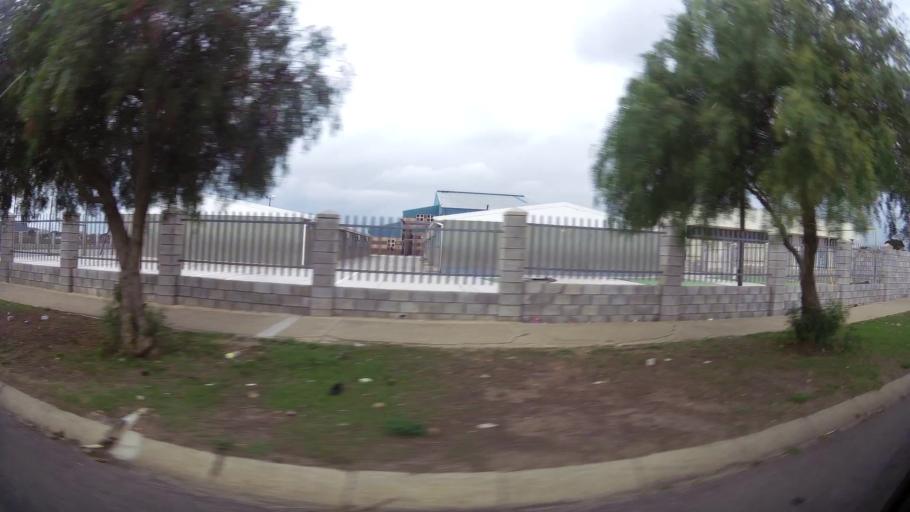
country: ZA
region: Eastern Cape
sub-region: Nelson Mandela Bay Metropolitan Municipality
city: Port Elizabeth
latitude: -33.8974
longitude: 25.5539
